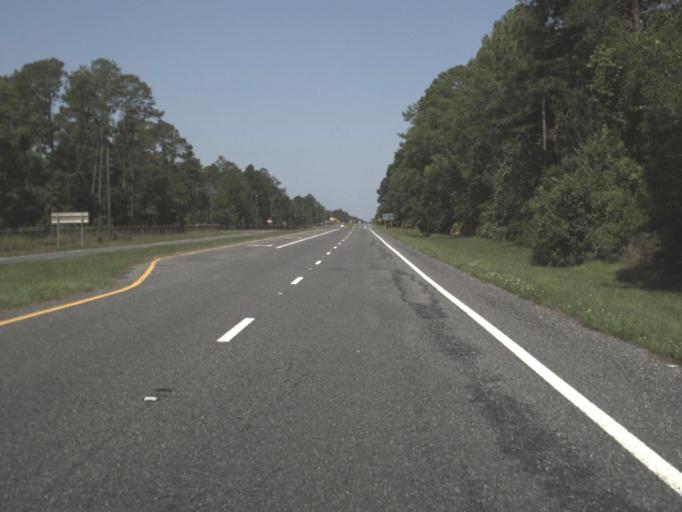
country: US
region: Florida
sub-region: Clay County
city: Middleburg
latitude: 29.9816
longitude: -81.9689
